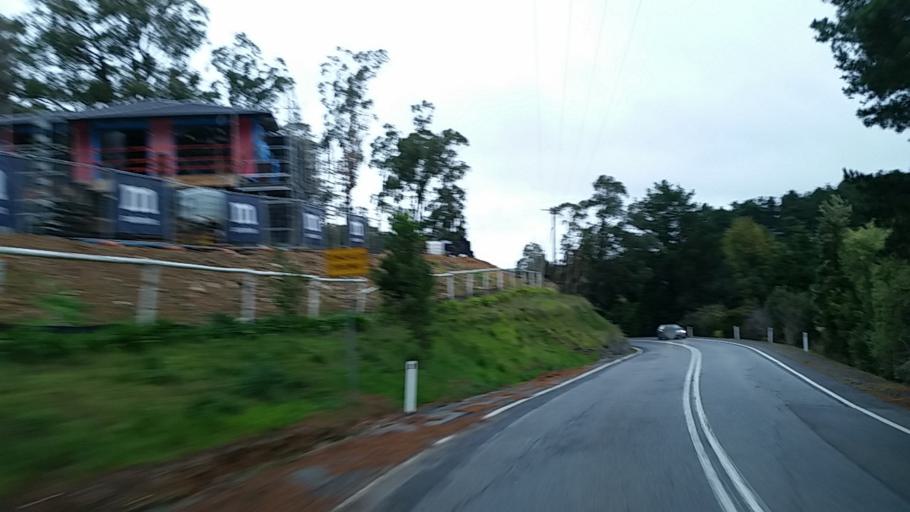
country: AU
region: South Australia
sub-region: Adelaide Hills
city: Bridgewater
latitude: -34.9617
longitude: 138.7355
